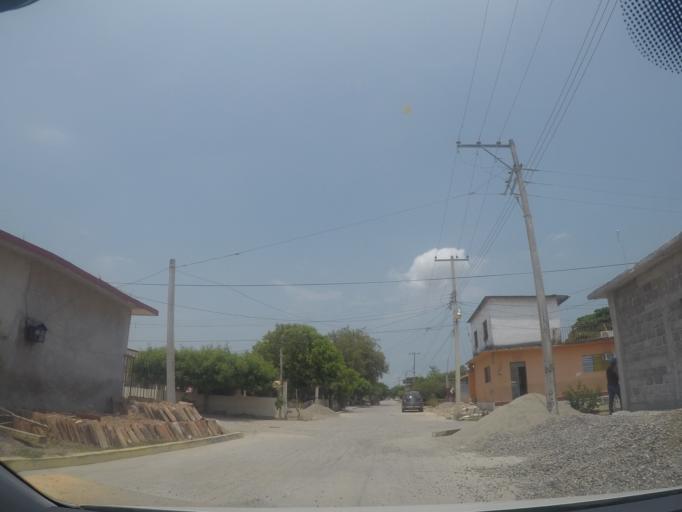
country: MX
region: Oaxaca
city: Asuncion Ixtaltepec
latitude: 16.5064
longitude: -95.0582
